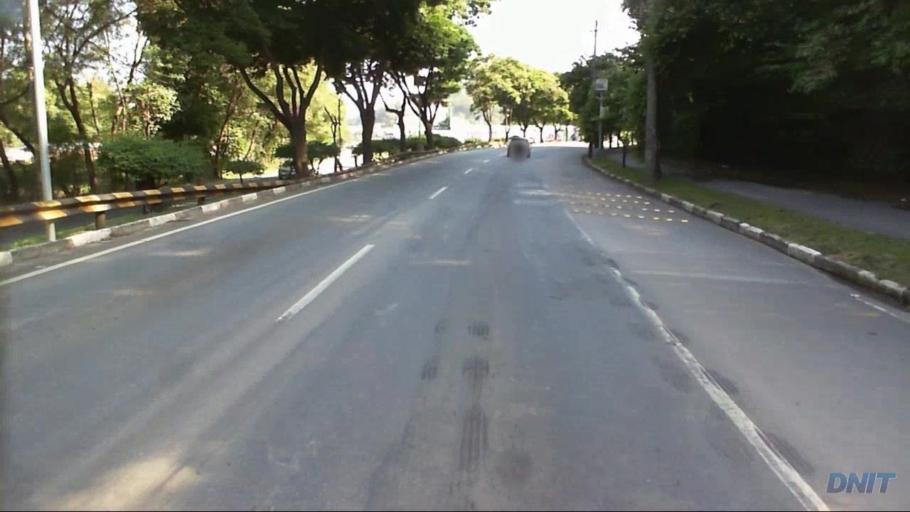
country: BR
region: Minas Gerais
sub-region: Ipatinga
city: Ipatinga
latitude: -19.4899
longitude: -42.5614
